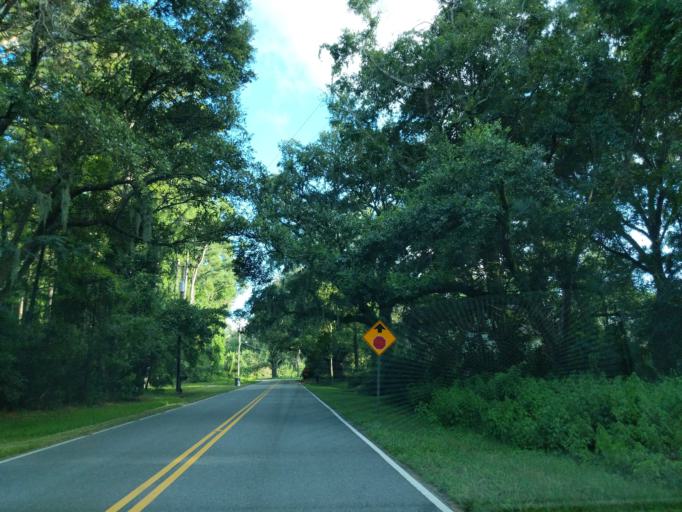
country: US
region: South Carolina
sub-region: Charleston County
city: Awendaw
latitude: 33.0941
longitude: -79.4654
